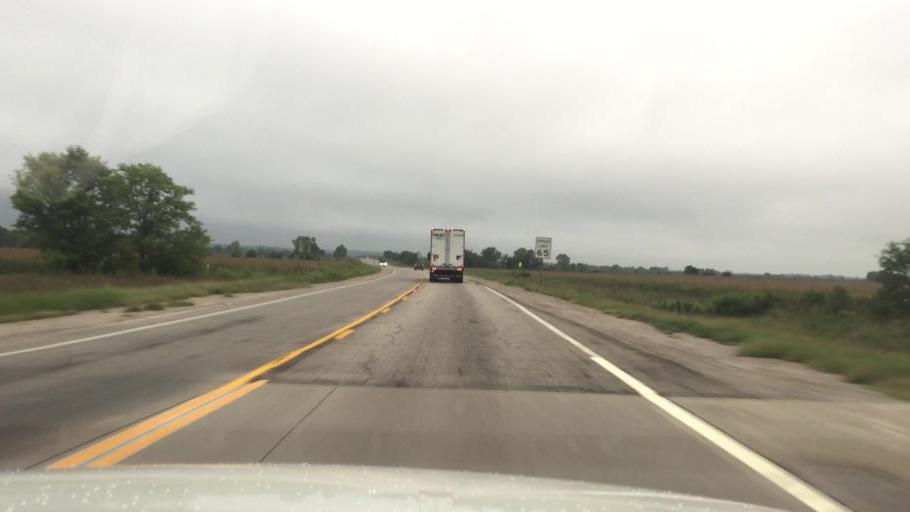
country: US
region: Kansas
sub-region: Montgomery County
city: Cherryvale
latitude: 37.2062
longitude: -95.5849
